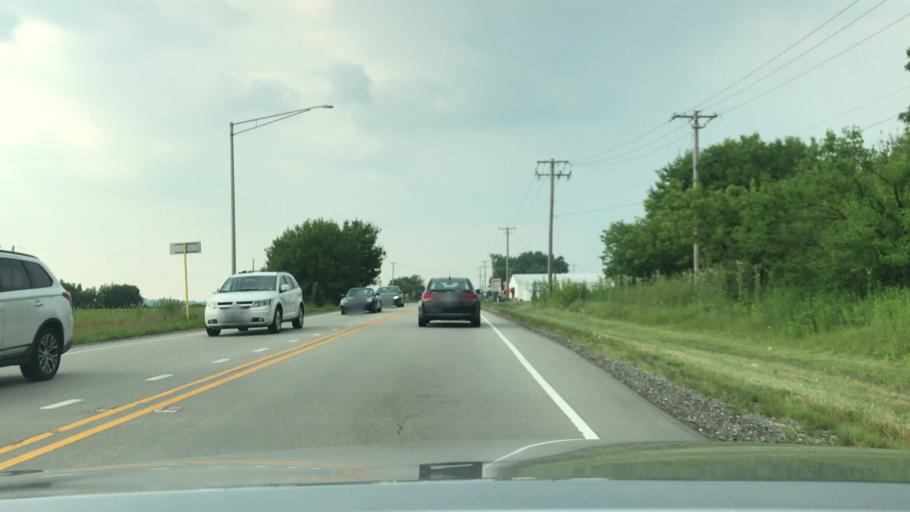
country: US
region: Illinois
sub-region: Will County
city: Plainfield
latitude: 41.6527
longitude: -88.2314
